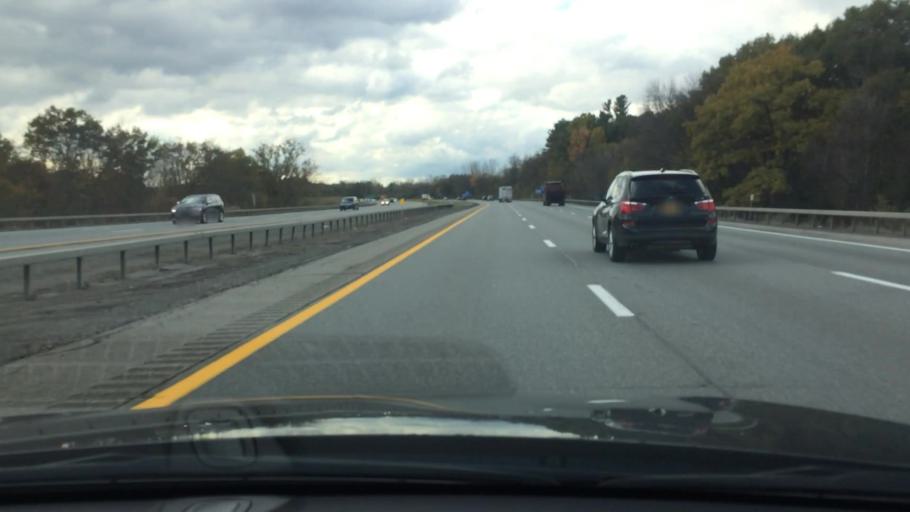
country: US
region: New York
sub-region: Saratoga County
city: Country Knolls
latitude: 42.9498
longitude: -73.8045
